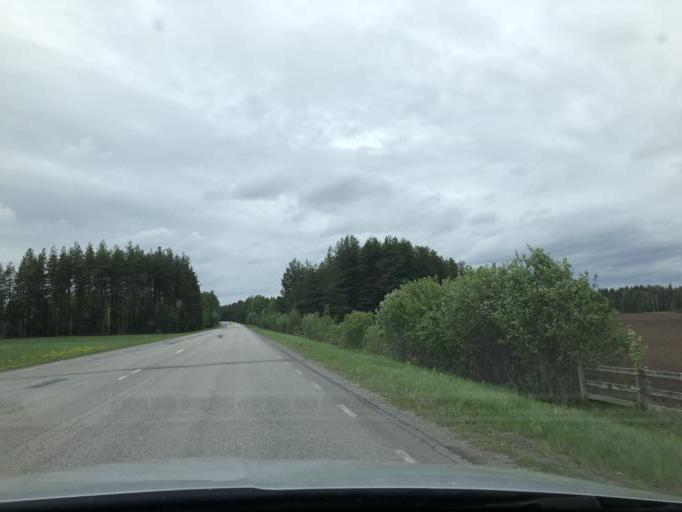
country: SE
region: Norrbotten
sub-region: Pitea Kommun
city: Bergsviken
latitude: 65.3572
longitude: 21.3795
